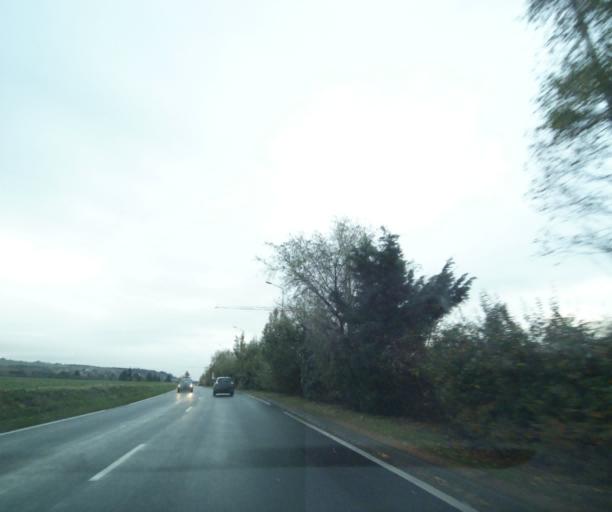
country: FR
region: Auvergne
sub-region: Departement du Puy-de-Dome
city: Perignat-les-Sarlieve
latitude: 45.7497
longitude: 3.1648
